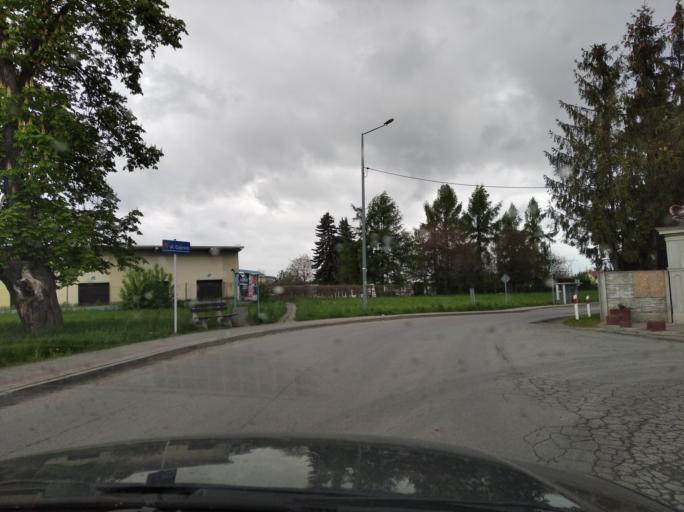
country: PL
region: Subcarpathian Voivodeship
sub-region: Powiat rzeszowski
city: Boguchwala
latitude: 49.9890
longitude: 21.9383
